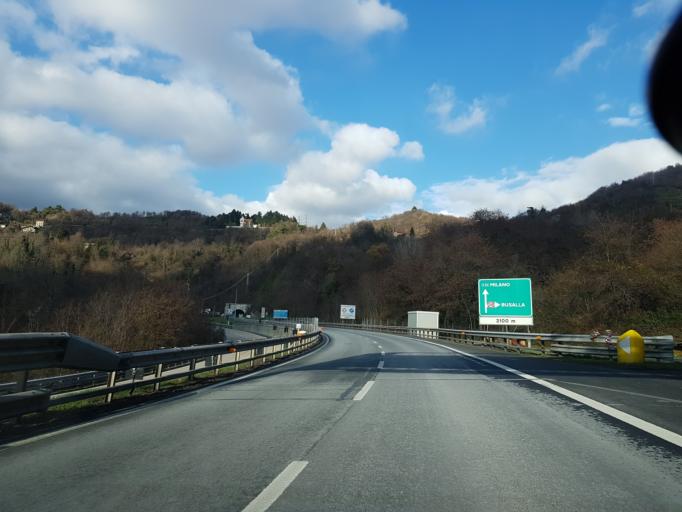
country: IT
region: Liguria
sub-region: Provincia di Genova
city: Busalla
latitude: 44.5477
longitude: 8.9449
